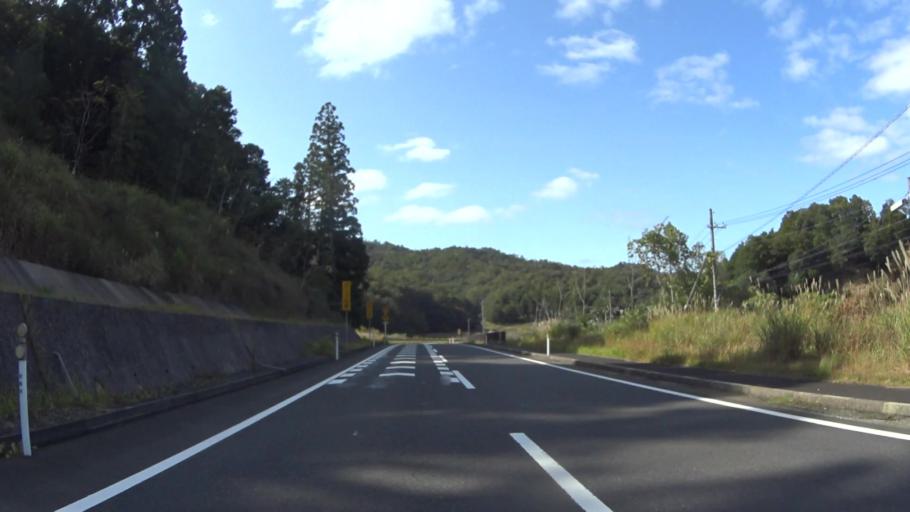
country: JP
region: Hyogo
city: Toyooka
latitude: 35.5653
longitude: 134.9760
